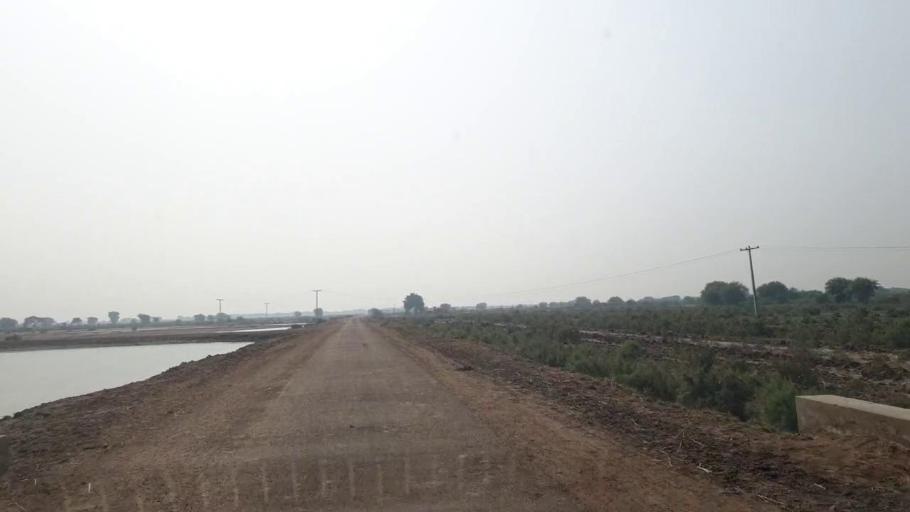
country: PK
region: Sindh
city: Matli
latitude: 25.1406
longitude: 68.6906
